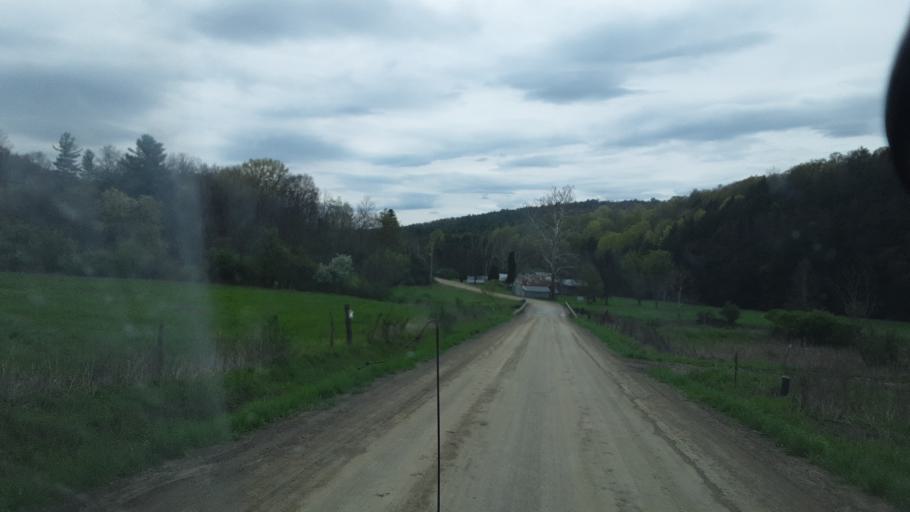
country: US
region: New York
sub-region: Steuben County
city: Addison
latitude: 42.1001
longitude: -77.3368
